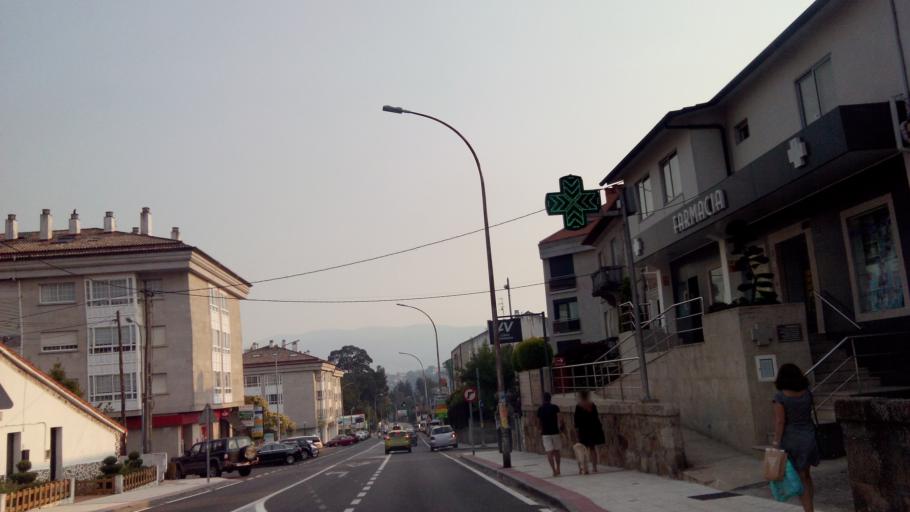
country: ES
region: Galicia
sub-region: Provincia de Pontevedra
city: Nigran
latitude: 42.1402
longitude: -8.8065
